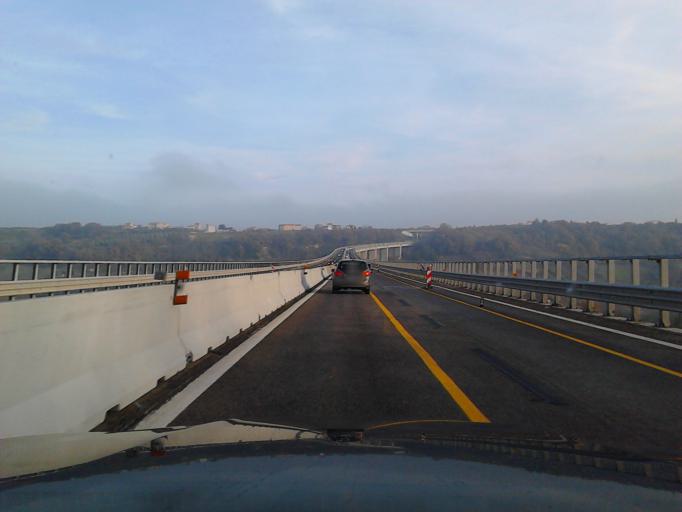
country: IT
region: Abruzzo
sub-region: Provincia di Chieti
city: Ortona
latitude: 42.3140
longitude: 14.4103
